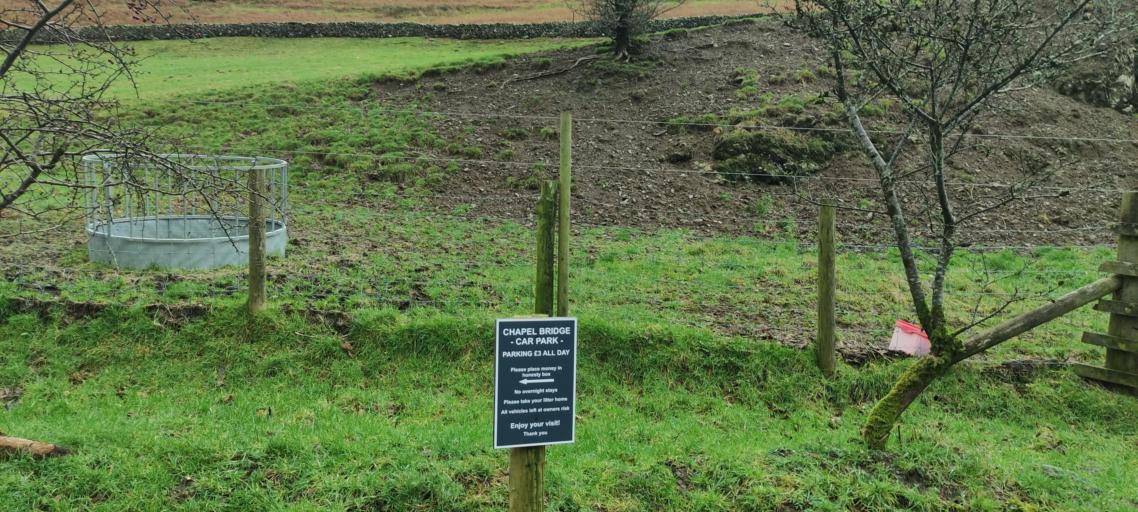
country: GB
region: England
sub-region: Cumbria
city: Keswick
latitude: 54.5639
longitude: -3.1898
